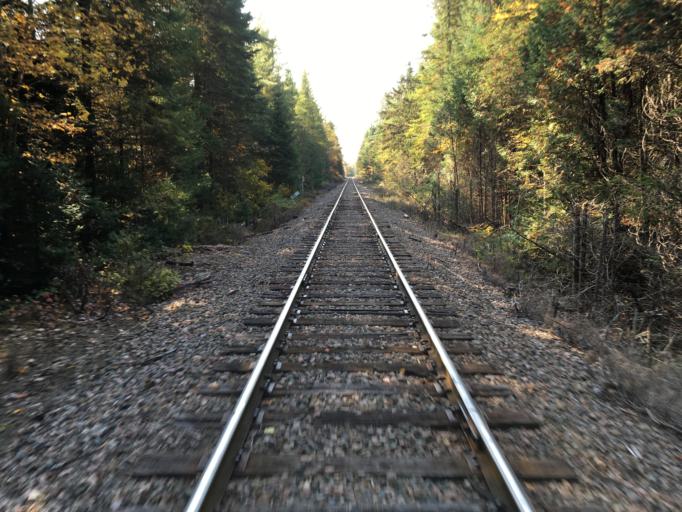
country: US
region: Vermont
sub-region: Caledonia County
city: Lyndonville
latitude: 44.6130
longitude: -71.9665
